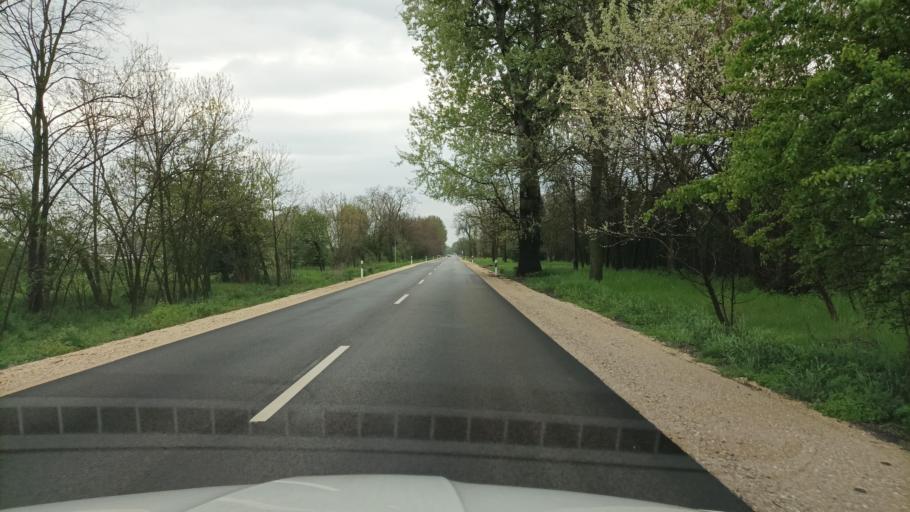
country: HU
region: Pest
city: Nagykoros
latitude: 47.0456
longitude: 19.7360
